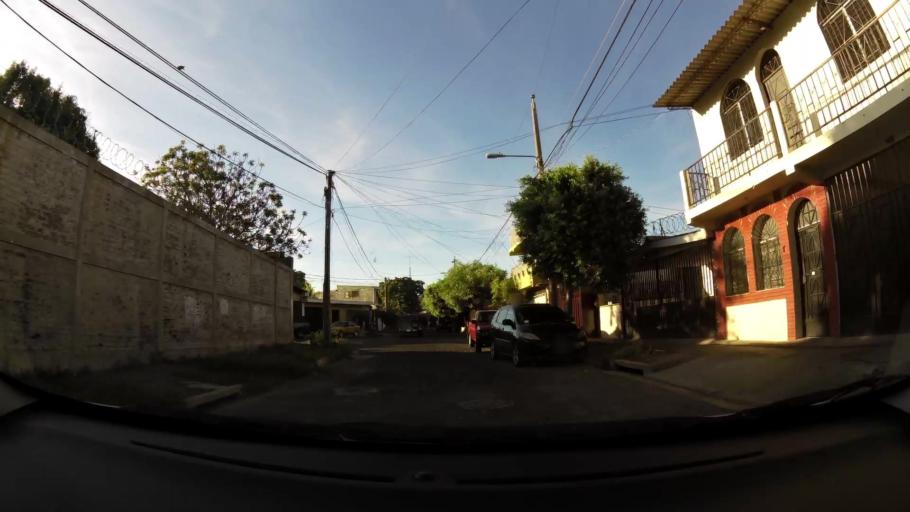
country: SV
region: San Miguel
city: San Miguel
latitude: 13.4605
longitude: -88.1625
